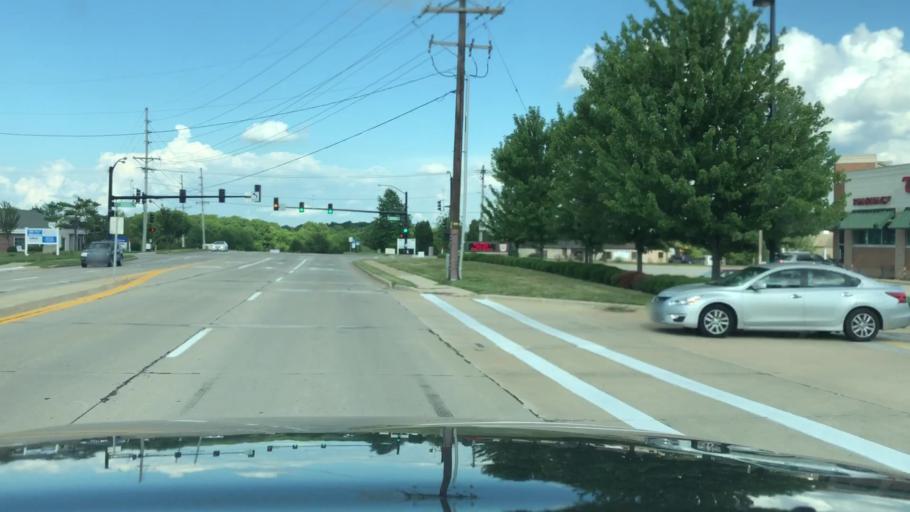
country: US
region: Missouri
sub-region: Saint Charles County
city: Wentzville
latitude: 38.8250
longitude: -90.8604
